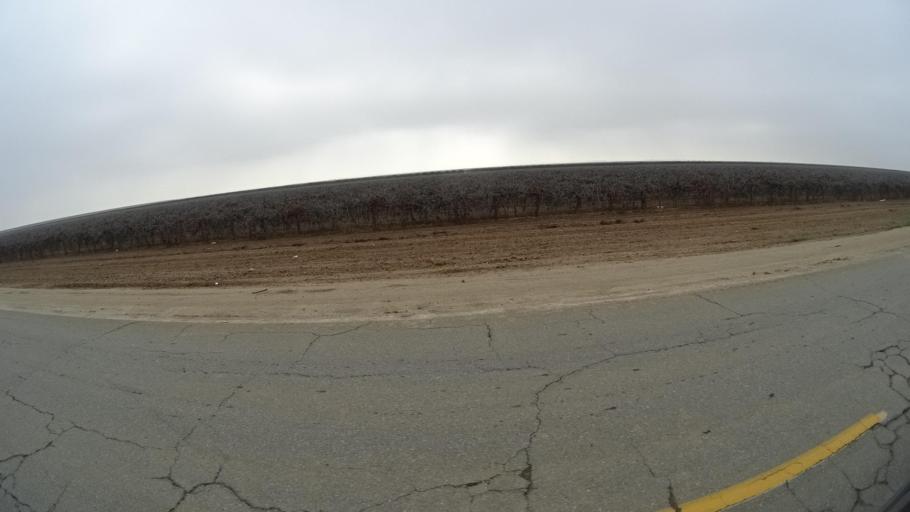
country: US
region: California
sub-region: Kern County
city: Maricopa
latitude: 35.0938
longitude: -119.2692
